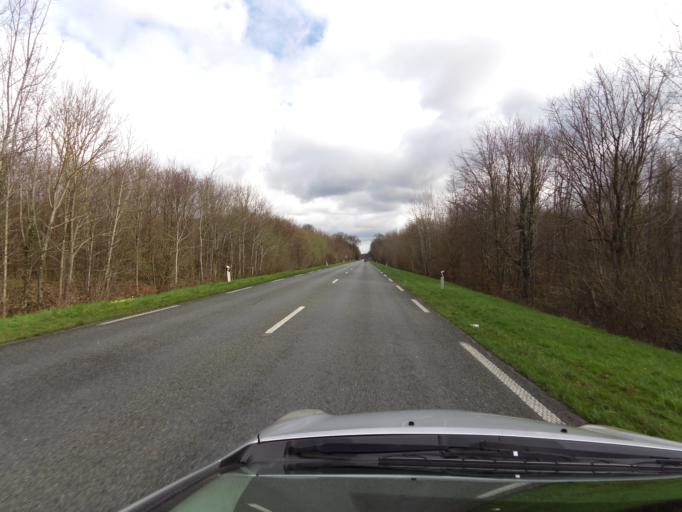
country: FR
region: Picardie
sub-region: Departement de l'Oise
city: Fleurines
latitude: 49.2788
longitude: 2.5960
